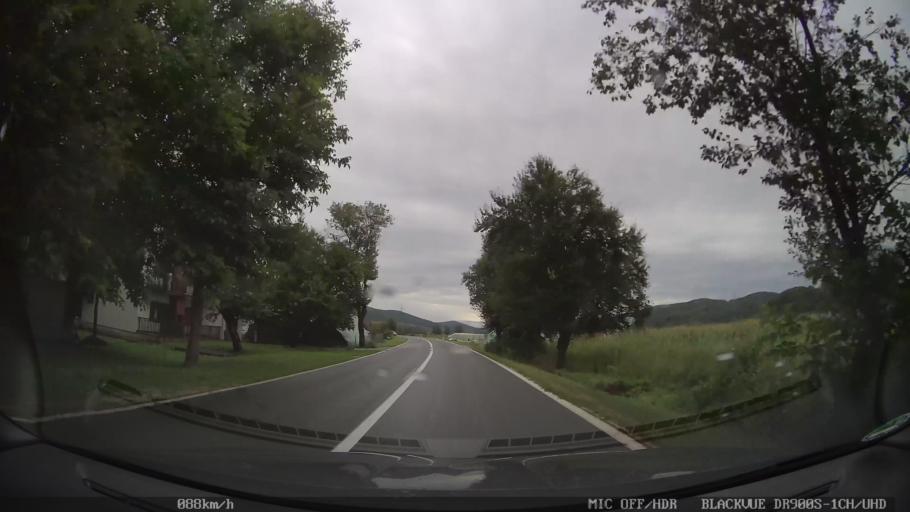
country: HR
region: Licko-Senjska
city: Brinje
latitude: 44.9207
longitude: 15.1452
